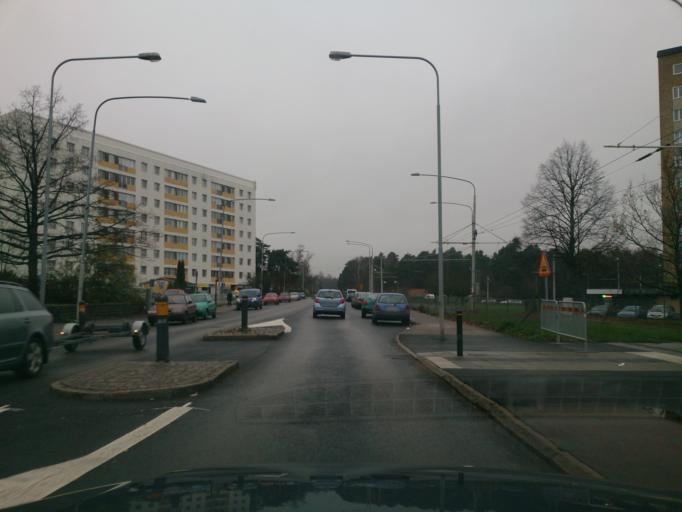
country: SE
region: OEstergoetland
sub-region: Norrkopings Kommun
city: Norrkoping
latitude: 58.6087
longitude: 16.1513
